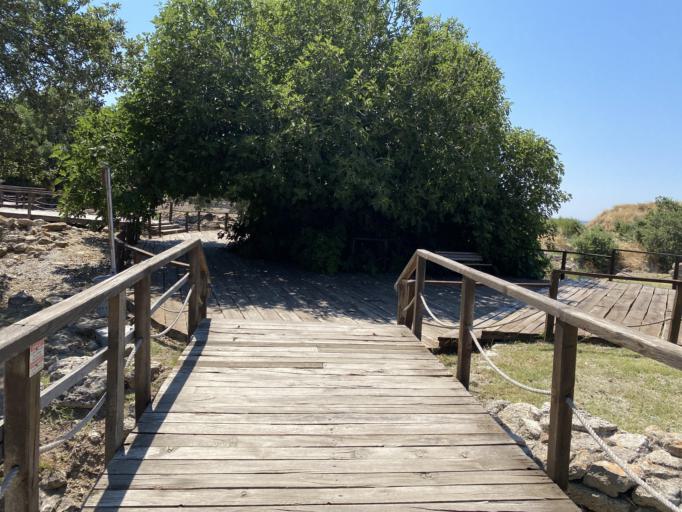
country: TR
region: Canakkale
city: Intepe
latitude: 39.9574
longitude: 26.2385
